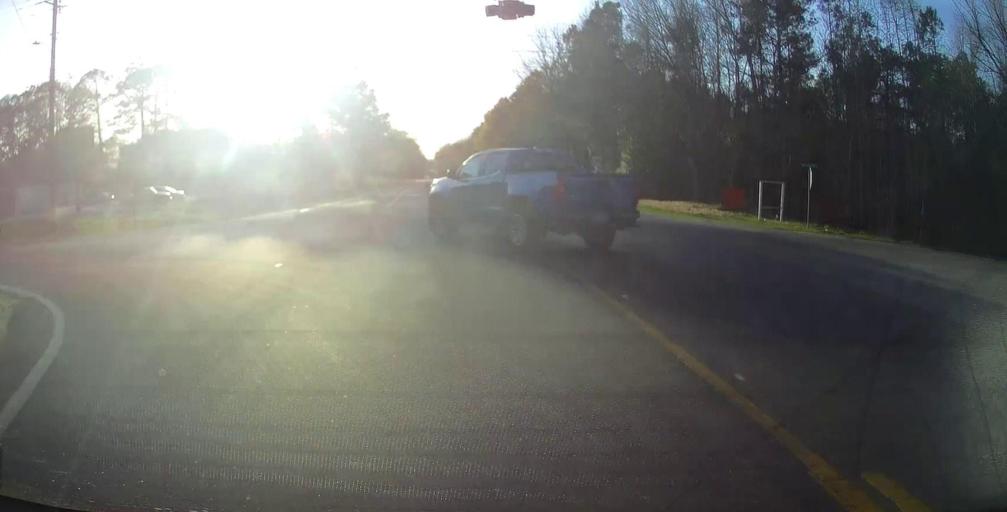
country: US
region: Georgia
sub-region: Evans County
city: Claxton
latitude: 32.1523
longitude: -81.8361
